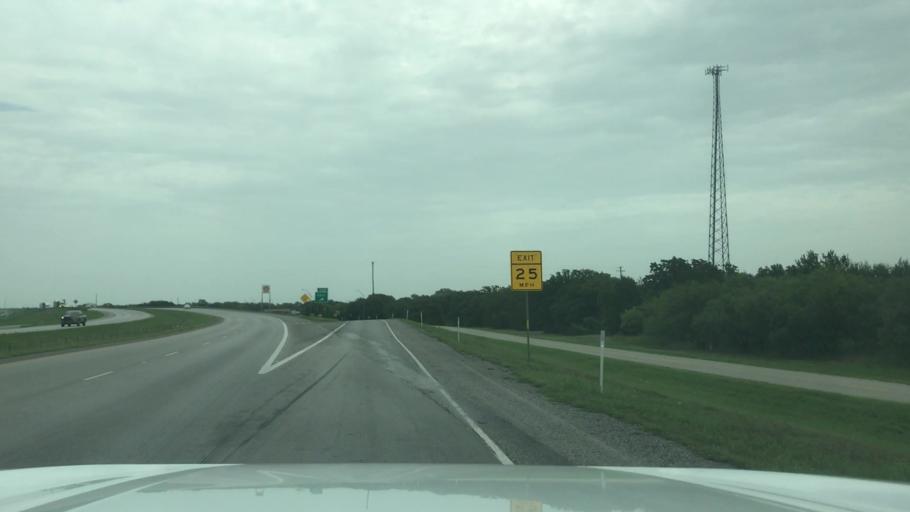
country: US
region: Texas
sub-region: Eastland County
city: Eastland
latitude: 32.3754
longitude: -98.8361
